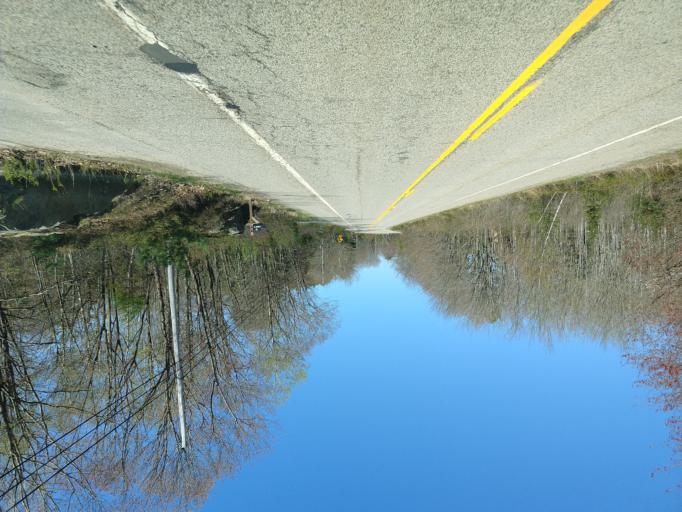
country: US
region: Maine
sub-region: York County
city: Biddeford
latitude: 43.4250
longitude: -70.3937
